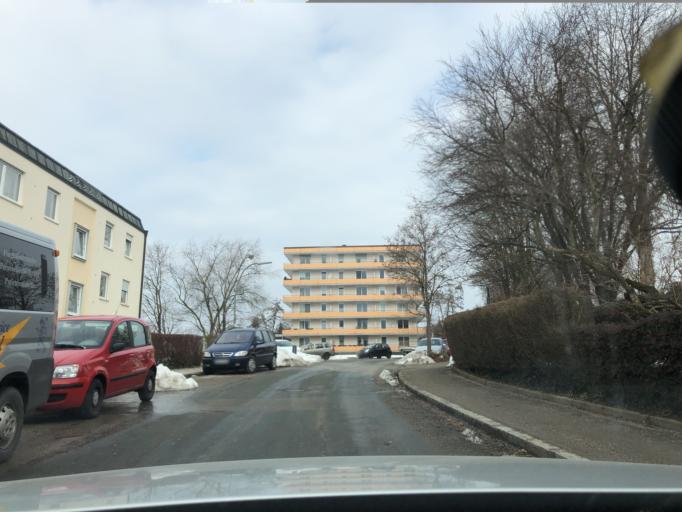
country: DE
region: Bavaria
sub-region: Upper Bavaria
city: Ebersberg
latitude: 48.0725
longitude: 11.9593
